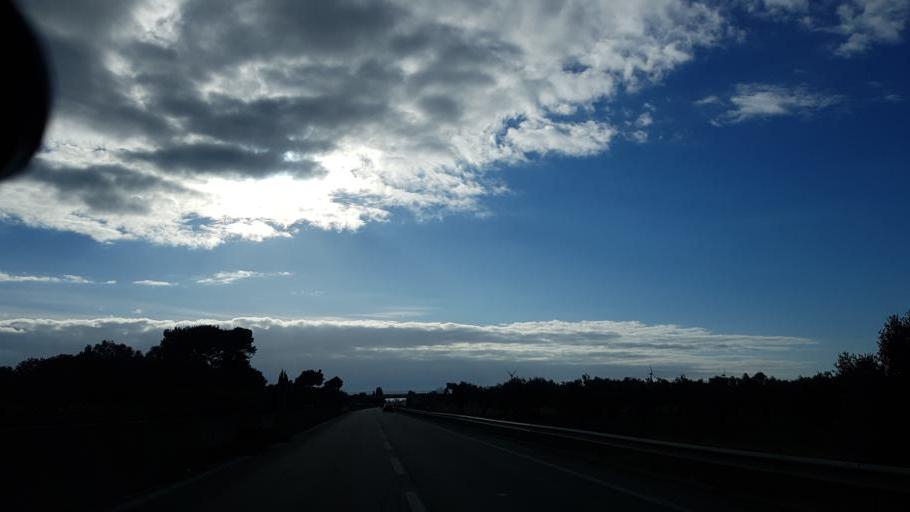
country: IT
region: Apulia
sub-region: Provincia di Brindisi
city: La Rosa
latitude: 40.5807
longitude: 17.9779
